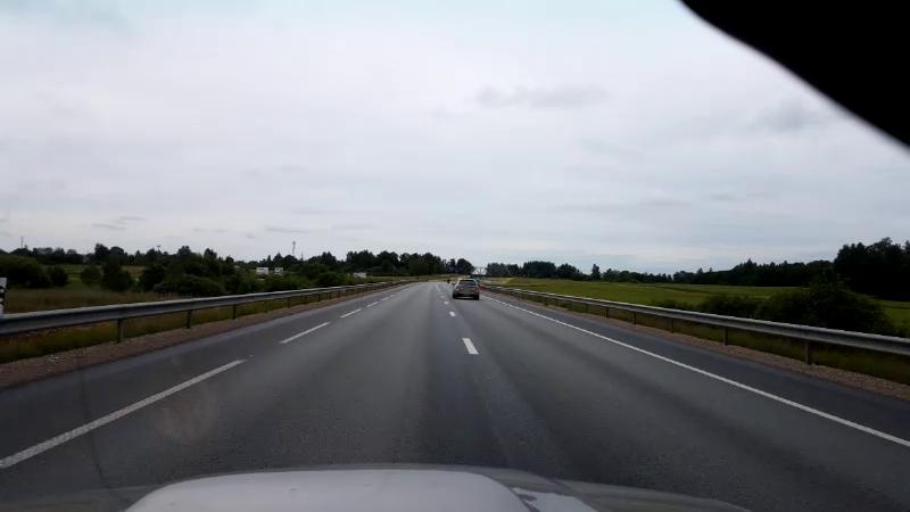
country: LV
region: Lecava
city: Iecava
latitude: 56.6351
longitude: 24.2246
